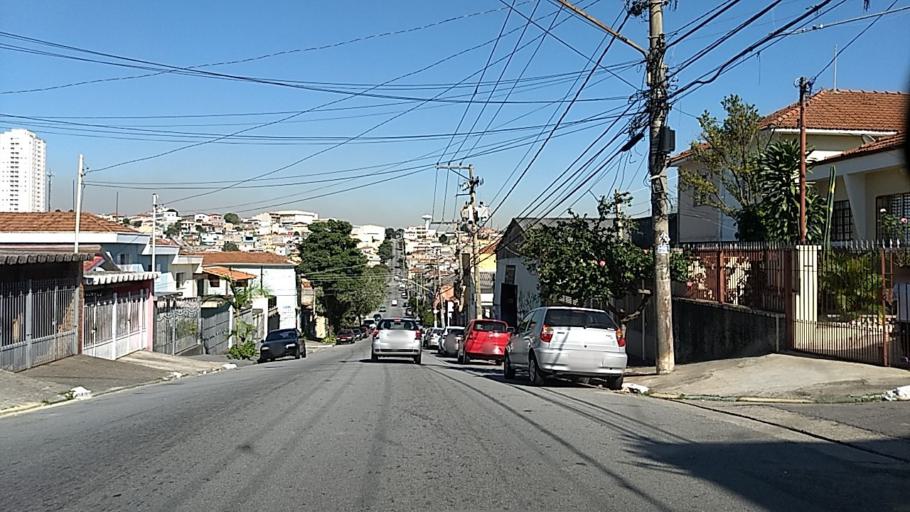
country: BR
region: Sao Paulo
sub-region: Guarulhos
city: Guarulhos
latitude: -23.4911
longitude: -46.5806
